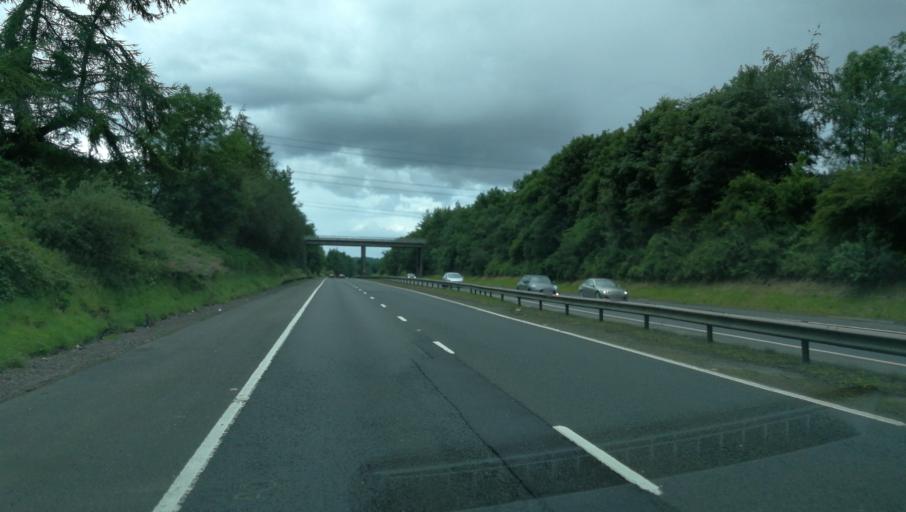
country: GB
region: Scotland
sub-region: Falkirk
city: Denny
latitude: 56.0070
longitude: -3.9169
